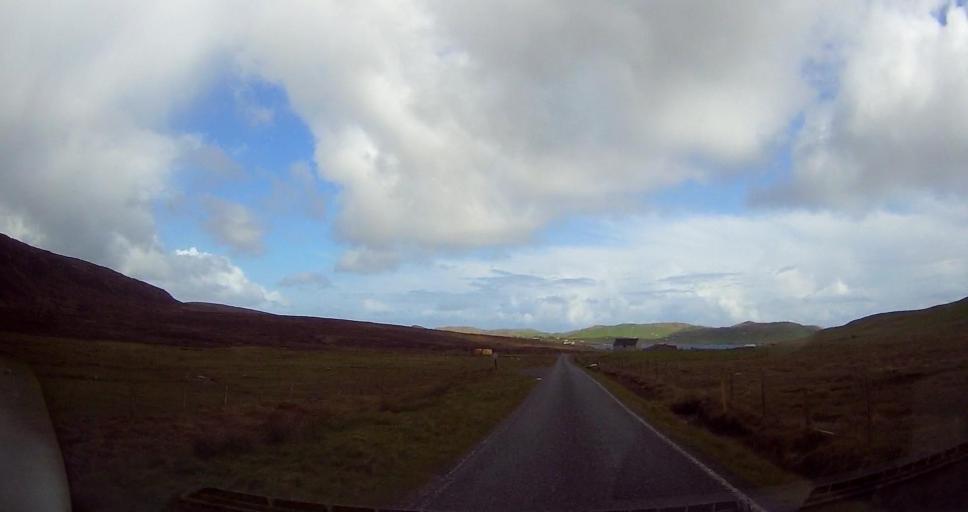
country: GB
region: Scotland
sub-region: Shetland Islands
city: Lerwick
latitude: 60.5688
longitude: -1.3339
